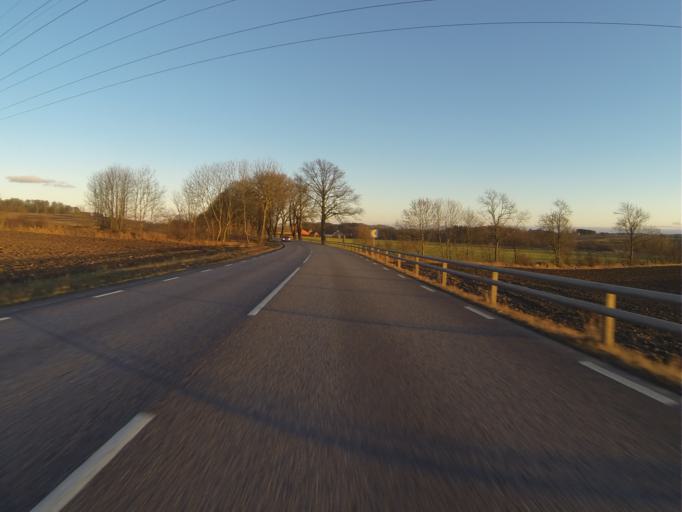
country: SE
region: Skane
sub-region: Eslovs Kommun
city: Eslov
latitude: 55.7818
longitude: 13.2772
